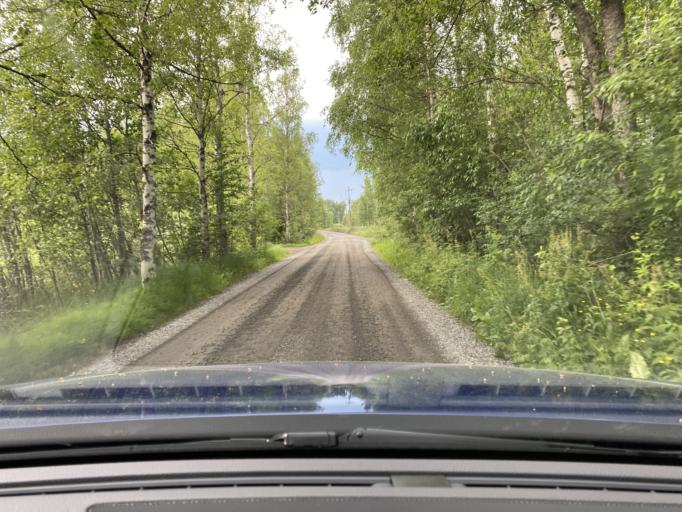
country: FI
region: Satakunta
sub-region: Rauma
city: Lappi
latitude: 61.1401
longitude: 21.9074
